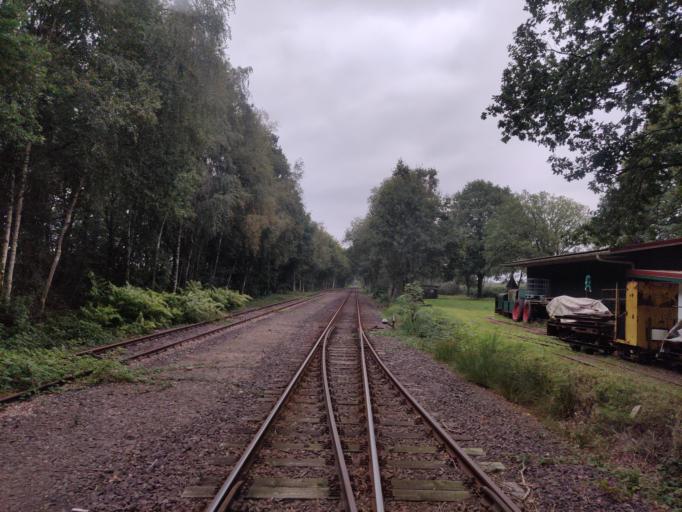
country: DE
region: Lower Saxony
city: Deinste
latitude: 53.5340
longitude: 9.4449
